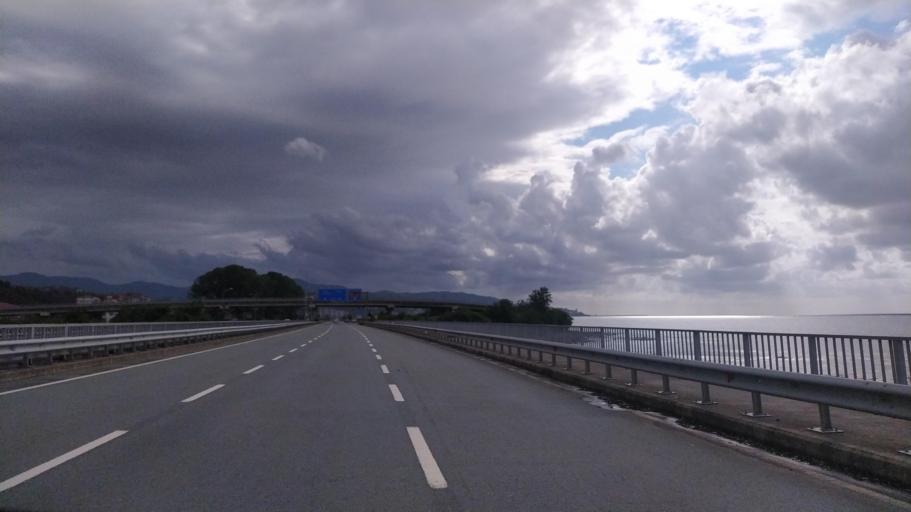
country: TR
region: Rize
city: Ardesen
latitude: 41.1892
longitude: 40.9627
